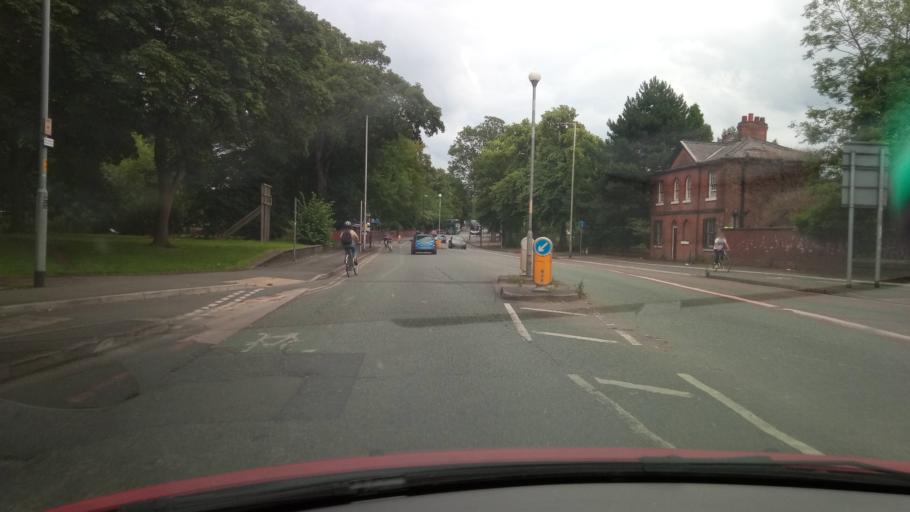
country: GB
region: England
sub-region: Manchester
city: Fallowfield
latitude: 53.4507
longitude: -2.2213
